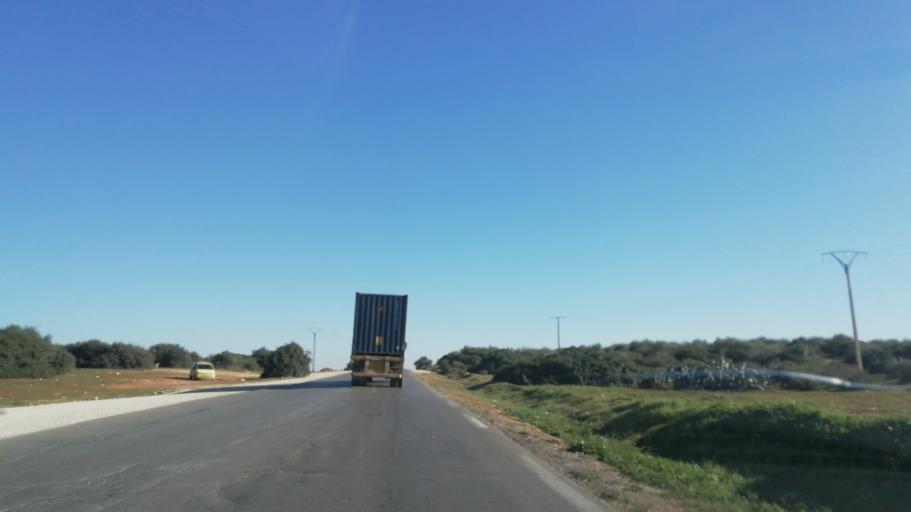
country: DZ
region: Relizane
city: Smala
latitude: 35.6916
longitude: 0.7893
